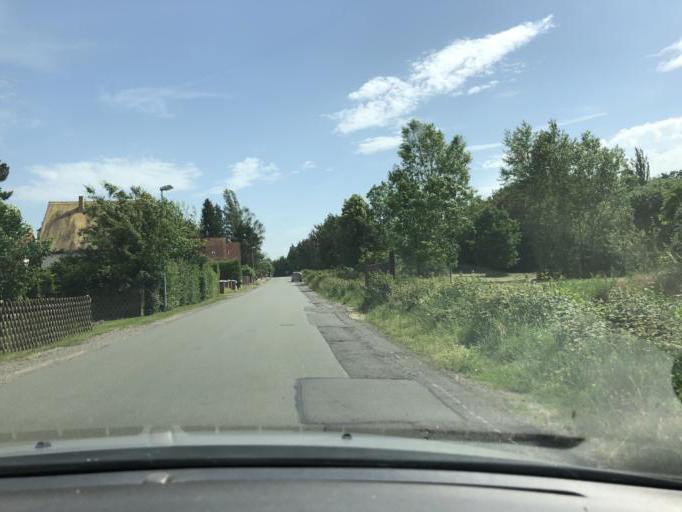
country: DE
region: Saxony
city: Borsdorf
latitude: 51.3622
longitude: 12.5212
